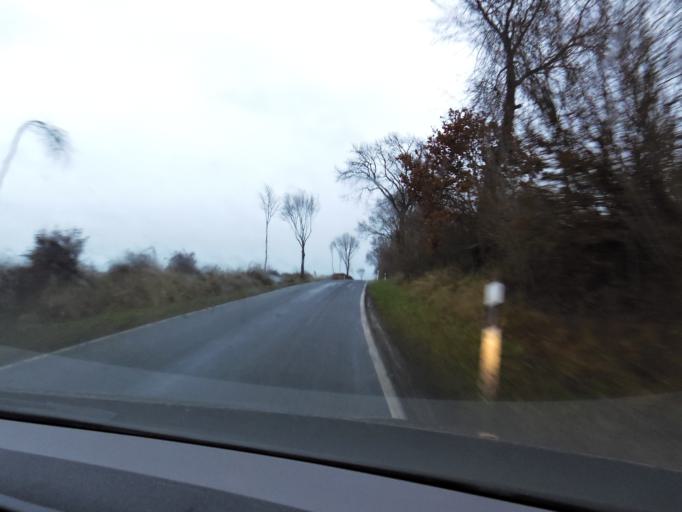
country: DE
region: Schleswig-Holstein
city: Mustin
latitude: 53.6793
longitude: 10.8931
